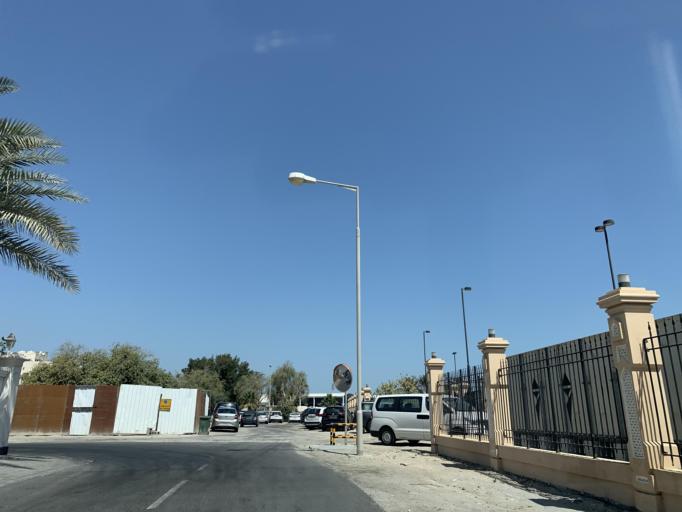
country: BH
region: Muharraq
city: Al Muharraq
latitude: 26.2667
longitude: 50.6192
